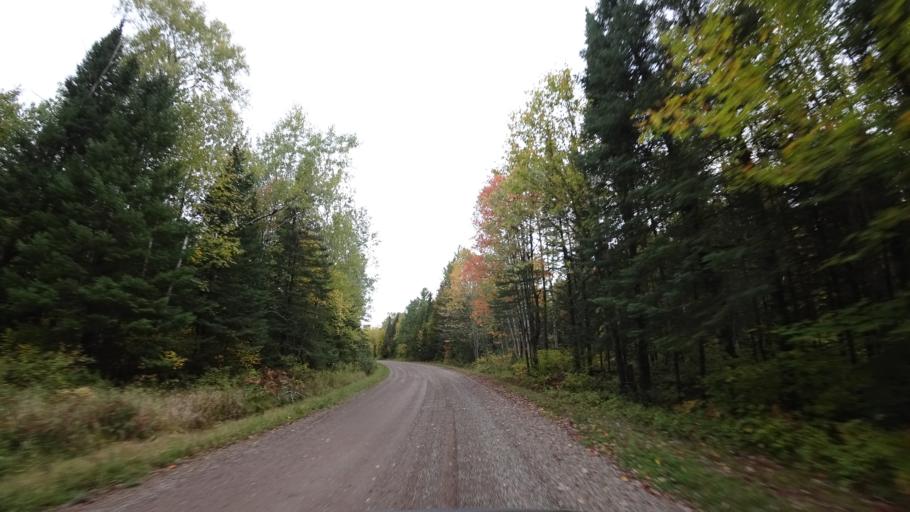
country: US
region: Wisconsin
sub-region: Sawyer County
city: Little Round Lake
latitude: 45.9699
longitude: -90.9805
